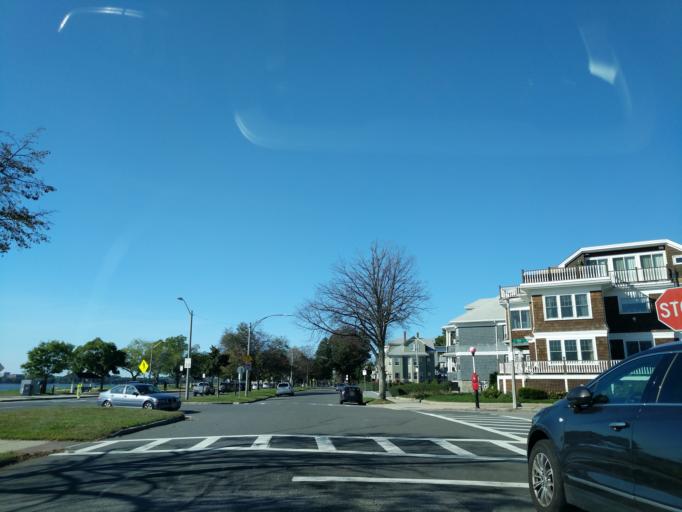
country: US
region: Massachusetts
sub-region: Suffolk County
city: South Boston
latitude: 42.3310
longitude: -71.0309
